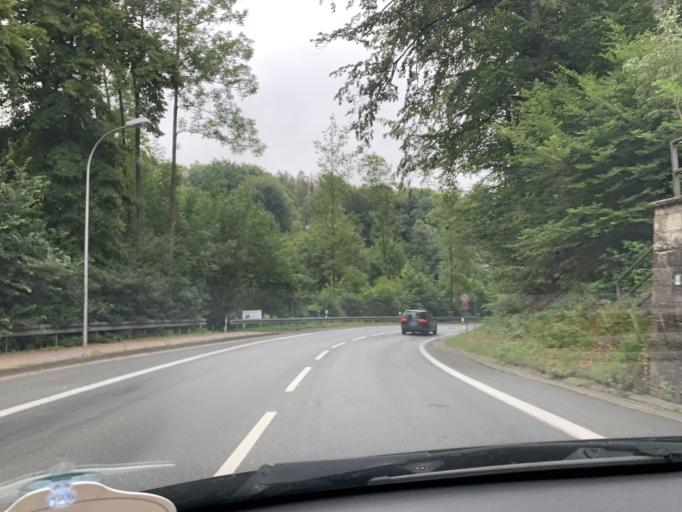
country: DE
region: North Rhine-Westphalia
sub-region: Regierungsbezirk Munster
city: Tecklenburg
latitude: 52.2179
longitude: 7.8216
